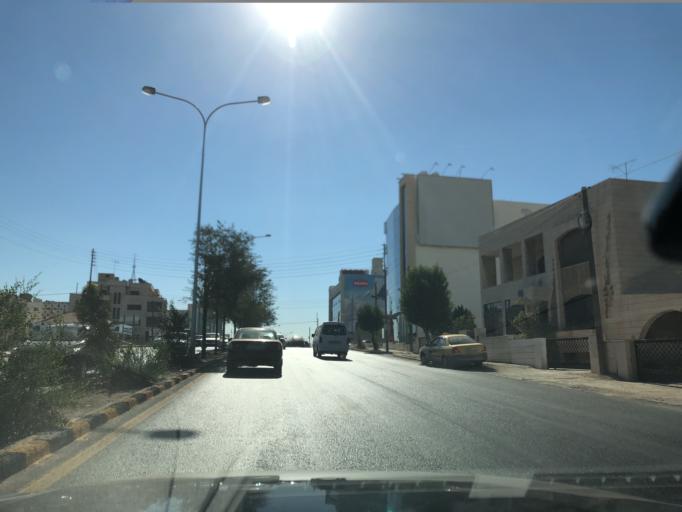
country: JO
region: Amman
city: Al Jubayhah
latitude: 31.9728
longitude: 35.8734
